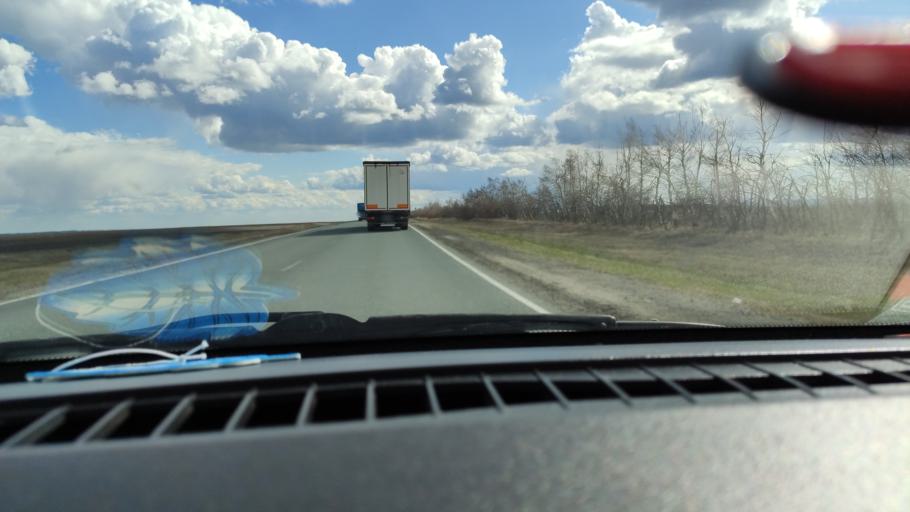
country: RU
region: Saratov
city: Dukhovnitskoye
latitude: 52.7912
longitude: 48.2321
